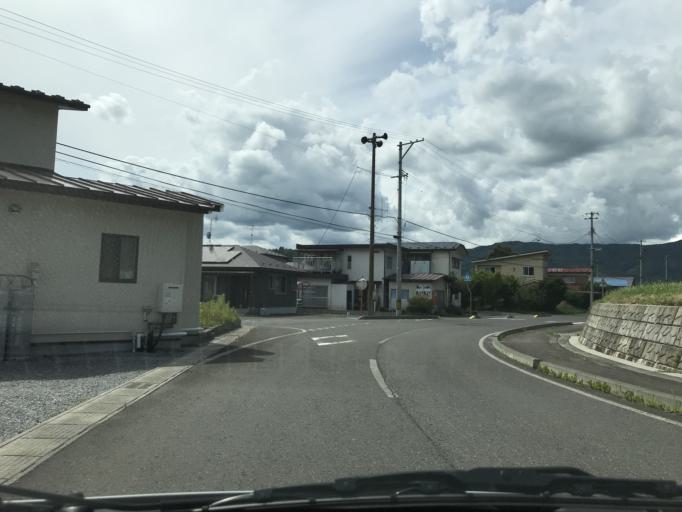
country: JP
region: Iwate
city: Tono
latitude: 39.3232
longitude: 141.5390
